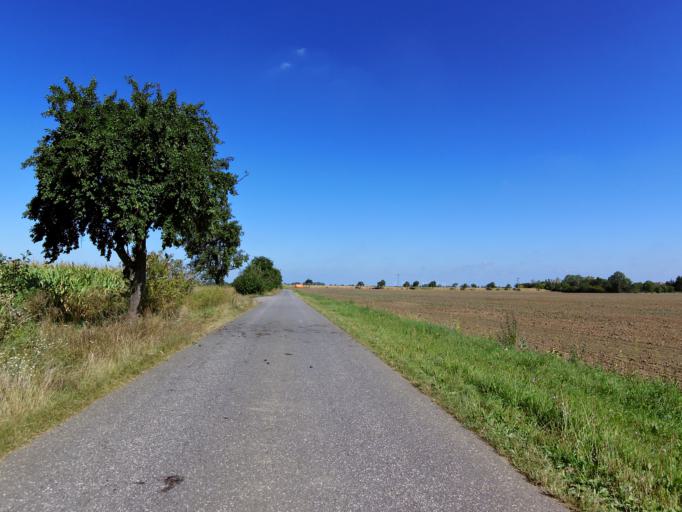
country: DE
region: Brandenburg
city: Muhlberg
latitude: 51.4010
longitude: 13.2435
